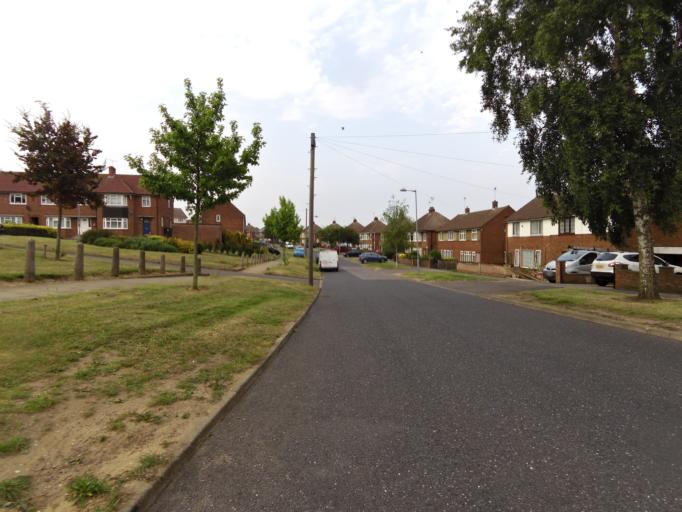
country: GB
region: England
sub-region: Suffolk
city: Ipswich
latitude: 52.0762
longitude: 1.1379
